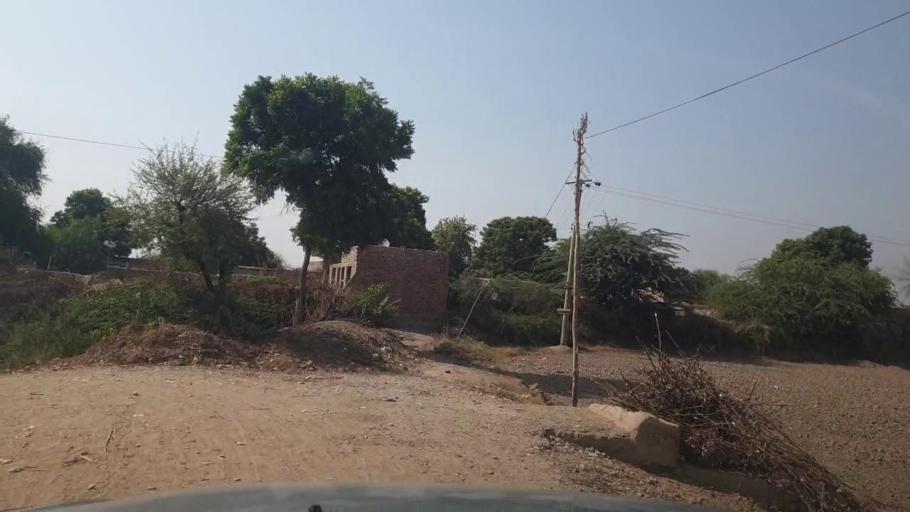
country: PK
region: Sindh
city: Bhit Shah
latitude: 25.7300
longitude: 68.4951
